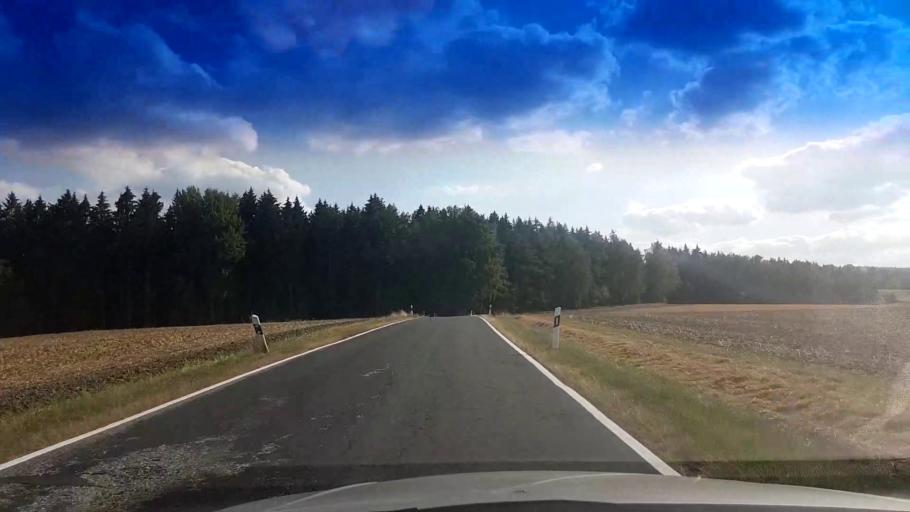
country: DE
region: Bavaria
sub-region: Upper Palatinate
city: Neualbenreuth
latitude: 49.9636
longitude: 12.4366
